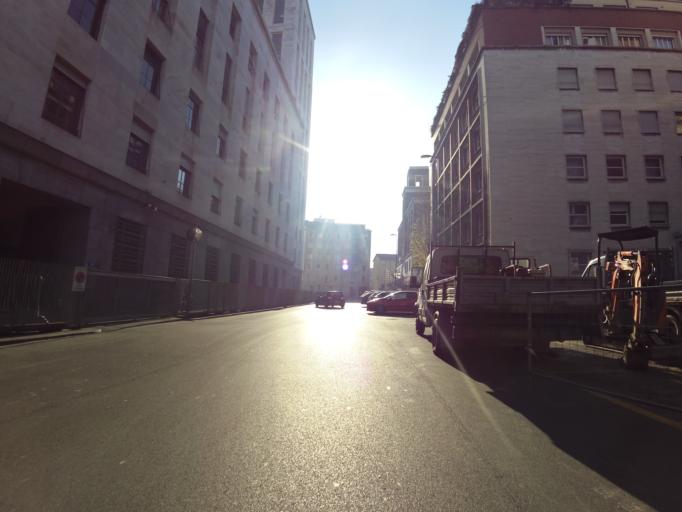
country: IT
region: Lombardy
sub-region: Citta metropolitana di Milano
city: Milano
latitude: 45.4608
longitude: 9.2002
